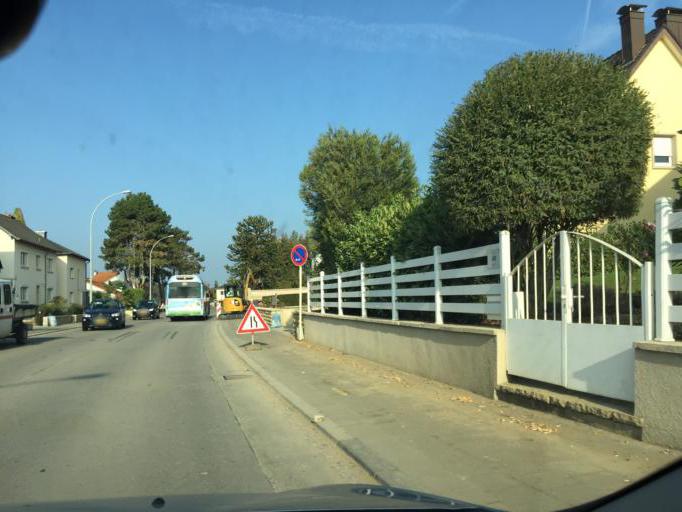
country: LU
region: Luxembourg
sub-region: Canton de Luxembourg
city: Contern
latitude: 49.5872
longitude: 6.2219
